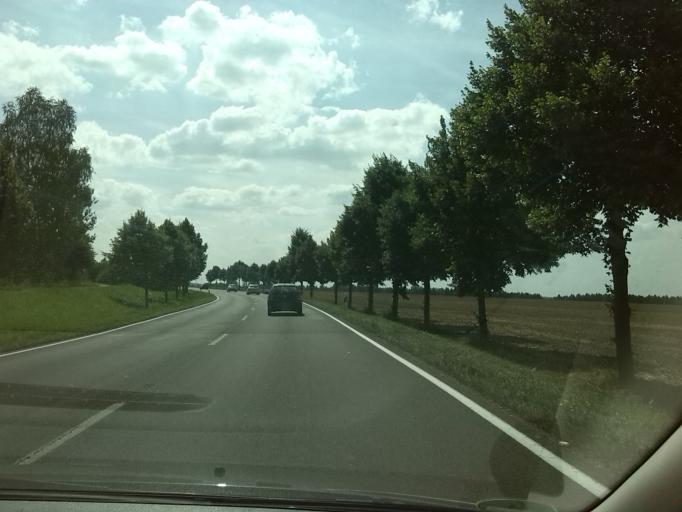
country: DE
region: Saxony
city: Borna
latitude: 51.1014
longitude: 12.4801
